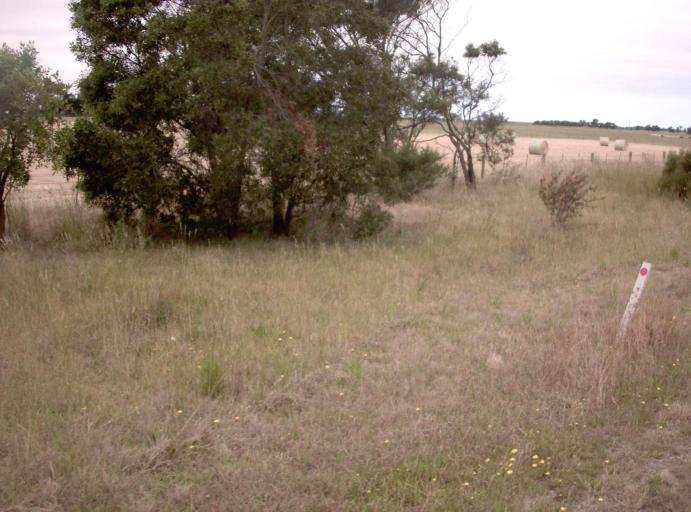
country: AU
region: Victoria
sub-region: Wellington
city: Sale
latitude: -38.5399
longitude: 146.9236
